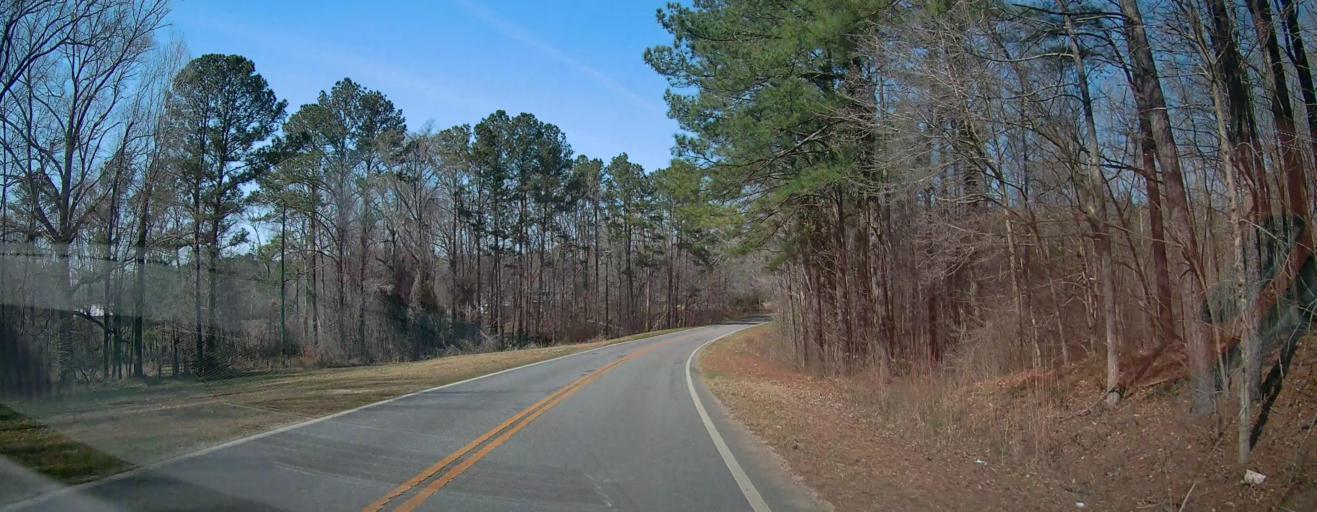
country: US
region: Georgia
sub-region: Jones County
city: Gray
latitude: 32.9487
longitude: -83.5431
